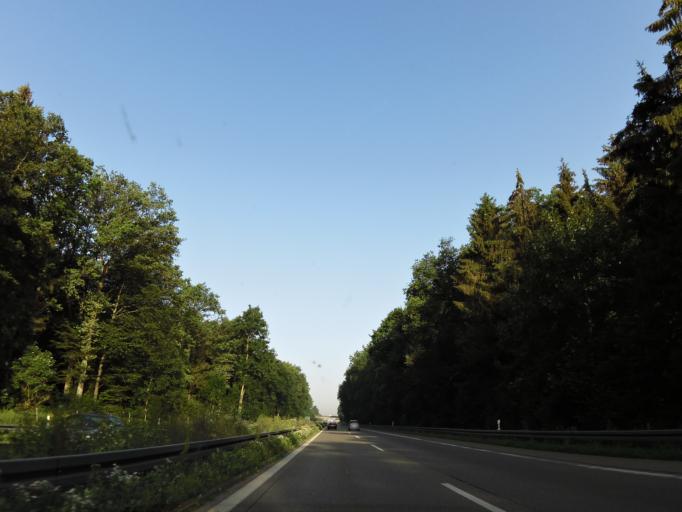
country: DE
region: Baden-Wuerttemberg
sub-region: Tuebingen Region
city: Beimerstetten
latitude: 48.4578
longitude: 10.0106
